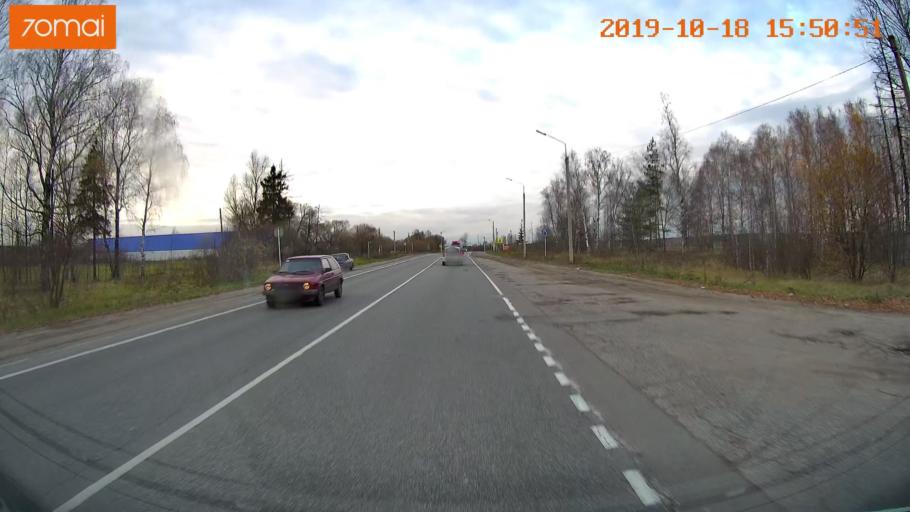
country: RU
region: Vladimir
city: Kommunar
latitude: 56.0366
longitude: 40.5548
